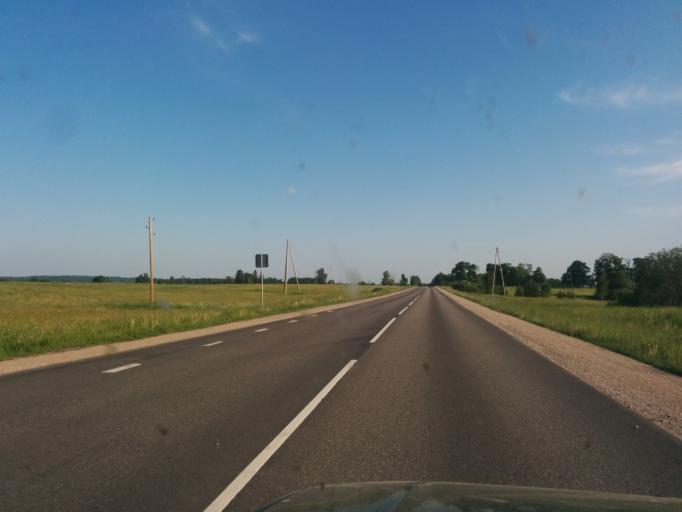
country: LV
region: Talsu Rajons
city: Talsi
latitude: 57.2862
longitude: 22.5732
